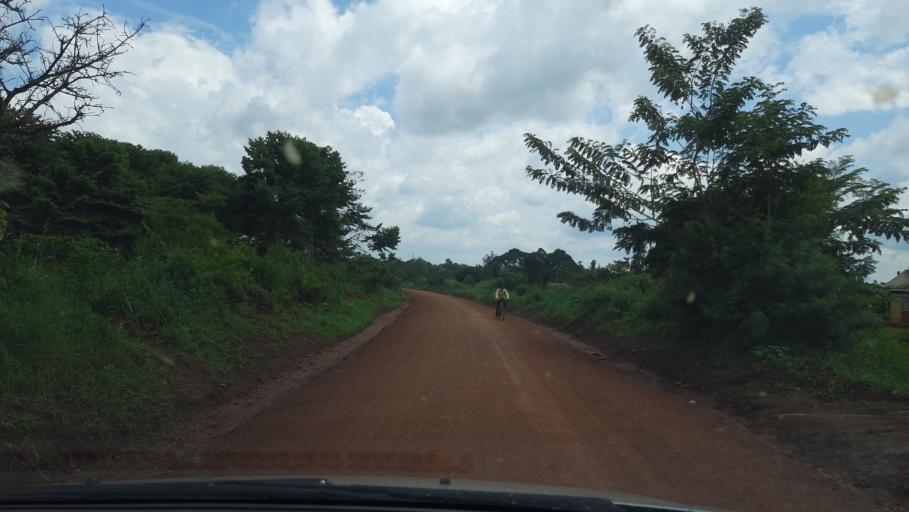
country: UG
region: Western Region
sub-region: Kiryandongo District
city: Kiryandongo
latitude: 1.8156
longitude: 31.9925
